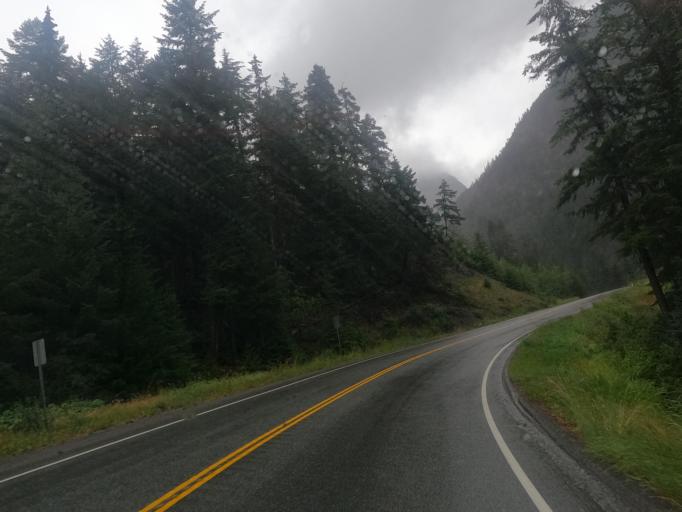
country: CA
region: British Columbia
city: Lillooet
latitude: 50.5343
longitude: -122.1396
